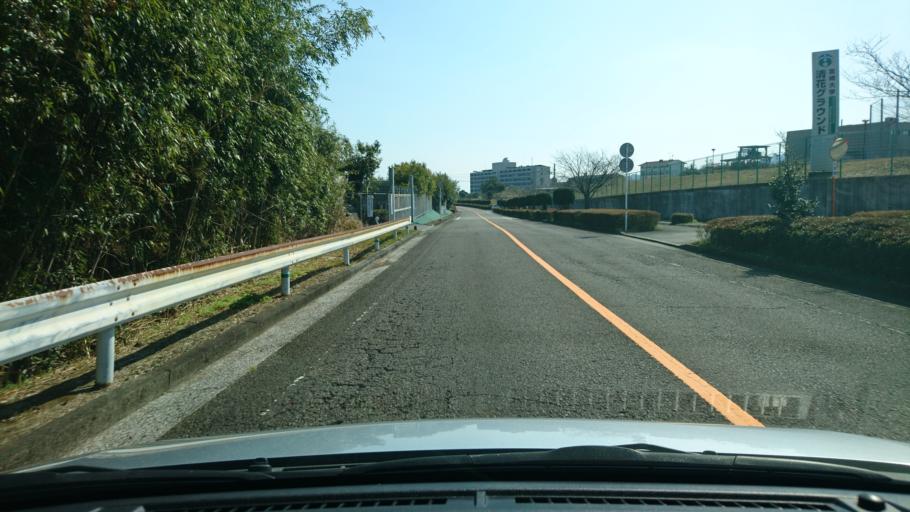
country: JP
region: Miyazaki
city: Miyazaki-shi
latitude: 31.8337
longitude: 131.4093
